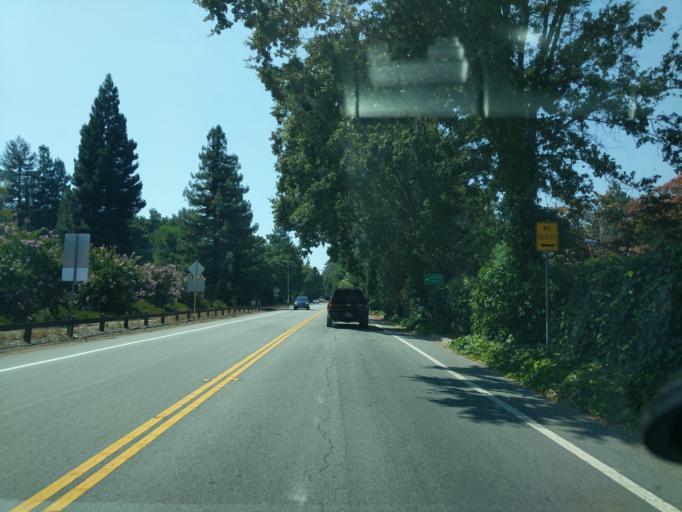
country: US
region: California
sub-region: Contra Costa County
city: Saranap
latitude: 37.8846
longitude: -122.0843
